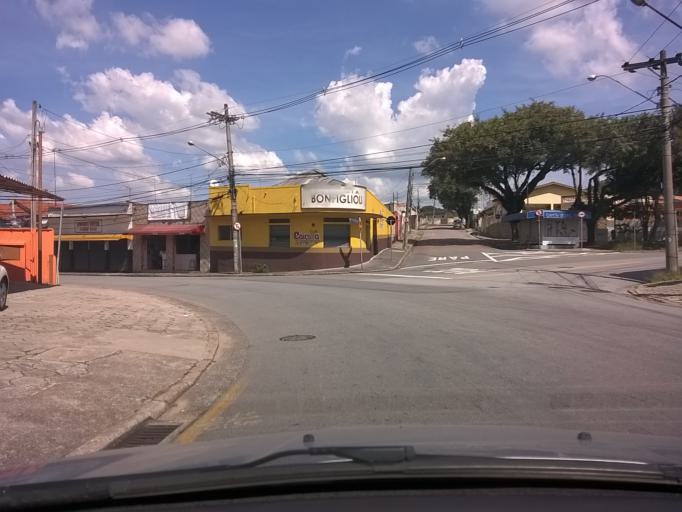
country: BR
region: Sao Paulo
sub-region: Jundiai
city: Jundiai
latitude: -23.2068
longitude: -46.8851
